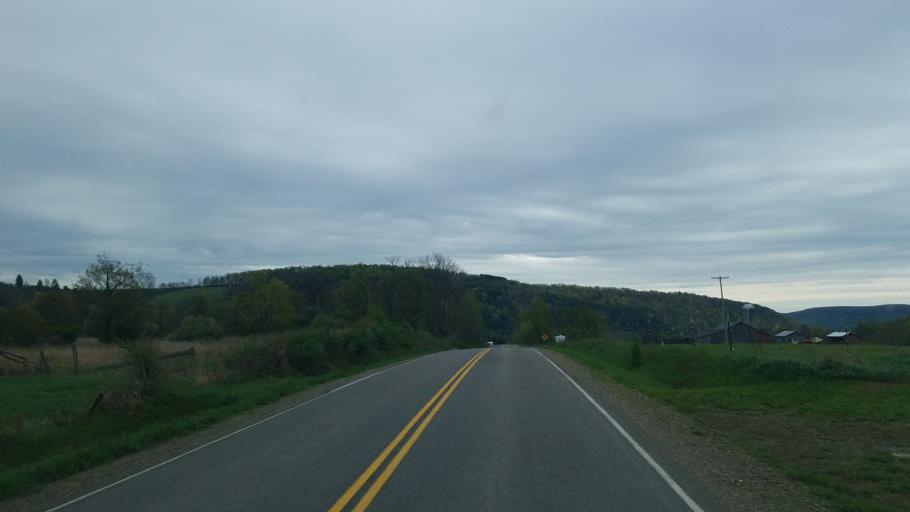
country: US
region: Pennsylvania
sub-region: Tioga County
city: Westfield
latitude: 42.0279
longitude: -77.4664
